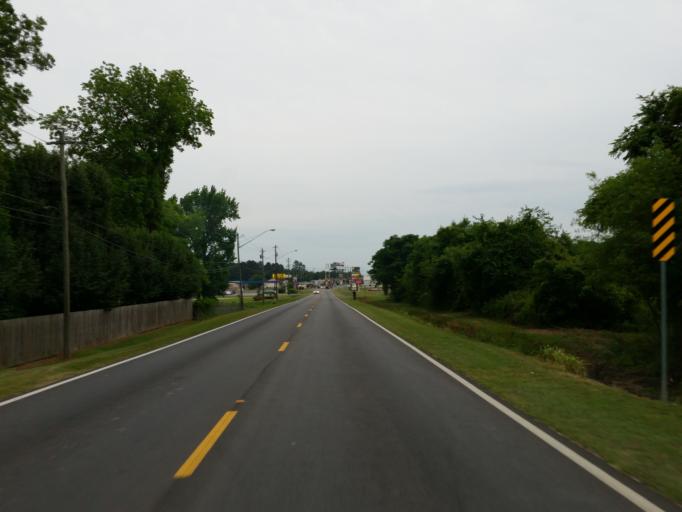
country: US
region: Georgia
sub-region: Dooly County
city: Unadilla
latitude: 32.2548
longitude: -83.7393
